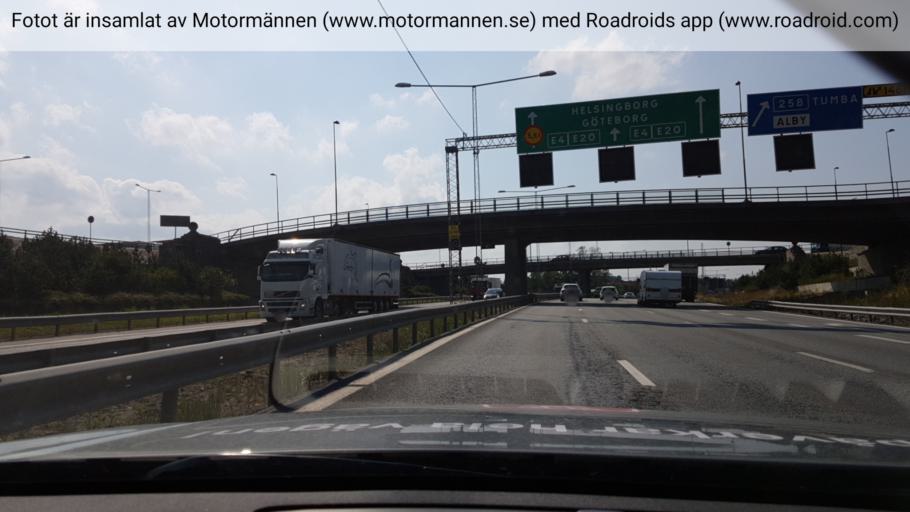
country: SE
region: Stockholm
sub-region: Botkyrka Kommun
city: Eriksberg
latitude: 59.2416
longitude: 17.8345
